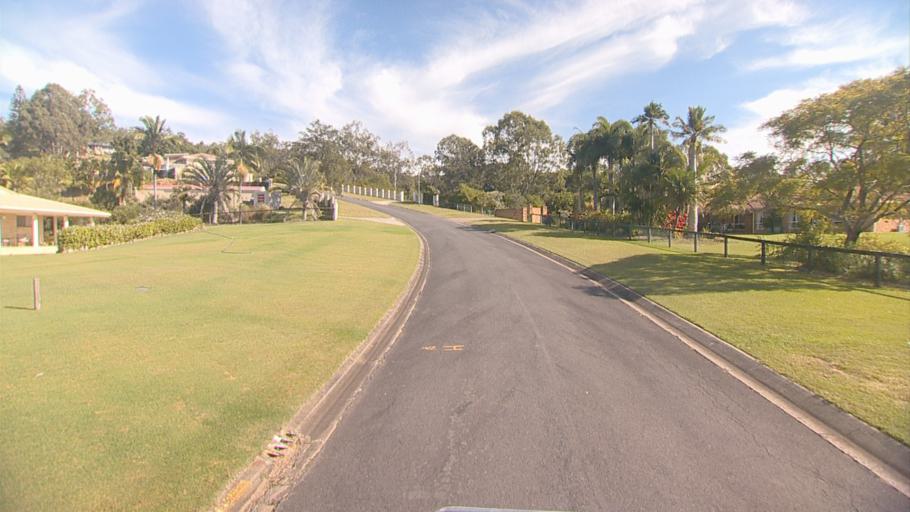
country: AU
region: Queensland
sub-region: Logan
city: Windaroo
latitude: -27.7592
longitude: 153.1808
